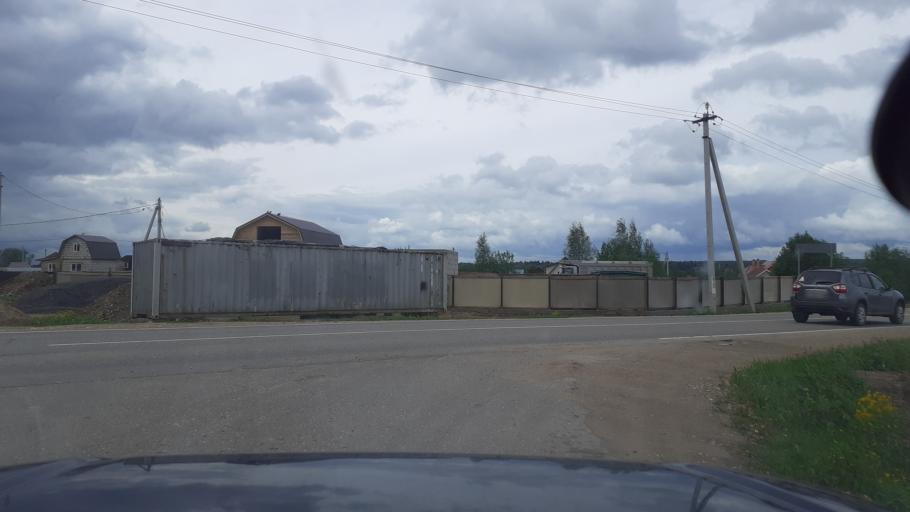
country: RU
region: Moskovskaya
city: Sychevo
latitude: 55.9654
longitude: 36.2312
